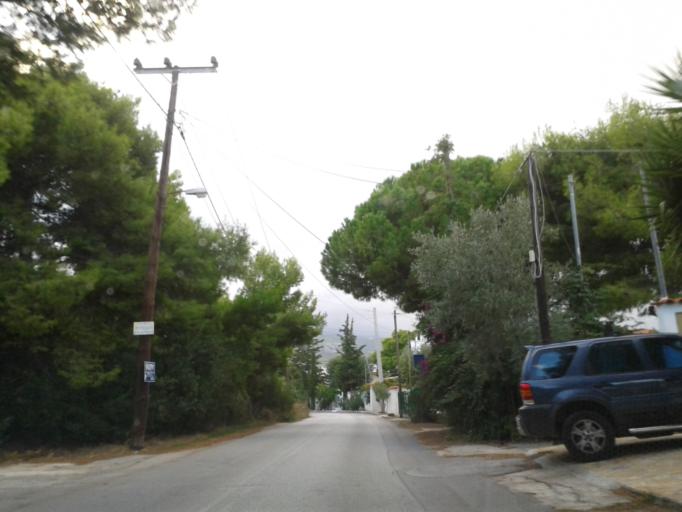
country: GR
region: Attica
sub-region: Nomarchia Anatolikis Attikis
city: Nea Makri
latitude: 38.0676
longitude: 23.9862
